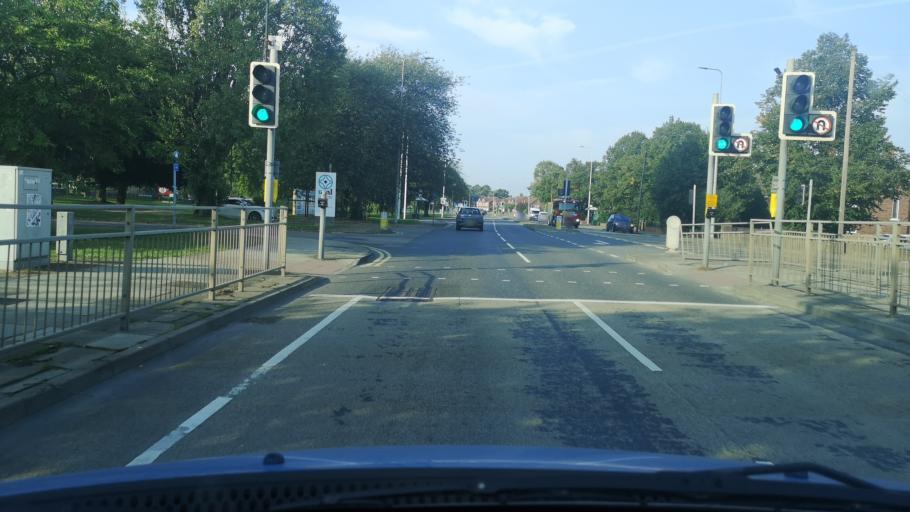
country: GB
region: England
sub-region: North Lincolnshire
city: Scunthorpe
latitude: 53.5802
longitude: -0.6544
